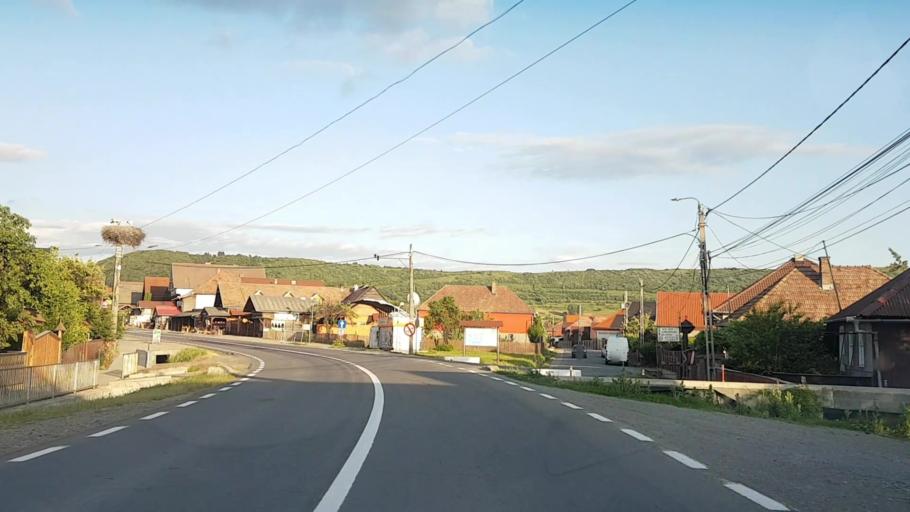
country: RO
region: Harghita
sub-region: Comuna Corund
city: Corund
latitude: 46.4741
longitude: 25.1782
